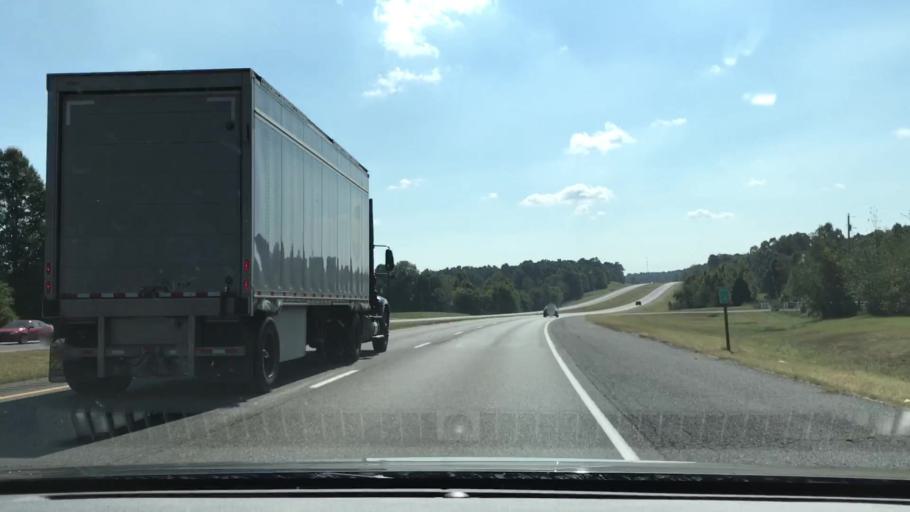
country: US
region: Kentucky
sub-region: Marshall County
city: Benton
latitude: 36.7873
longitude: -88.3272
